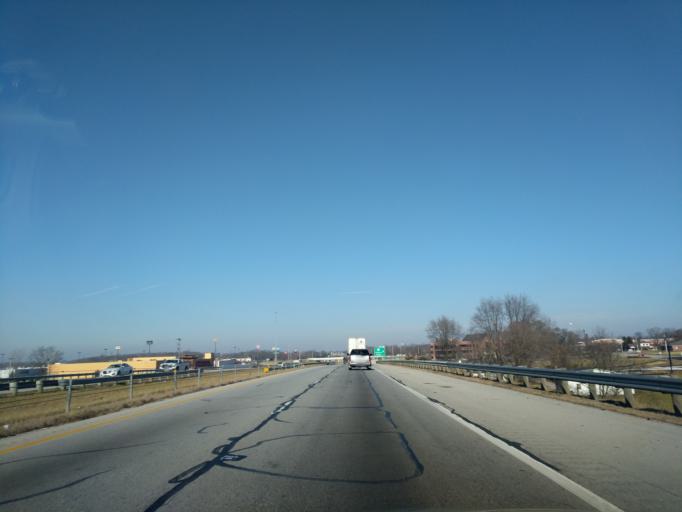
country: US
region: Ohio
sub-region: Miami County
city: Piqua
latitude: 40.1444
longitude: -84.2183
